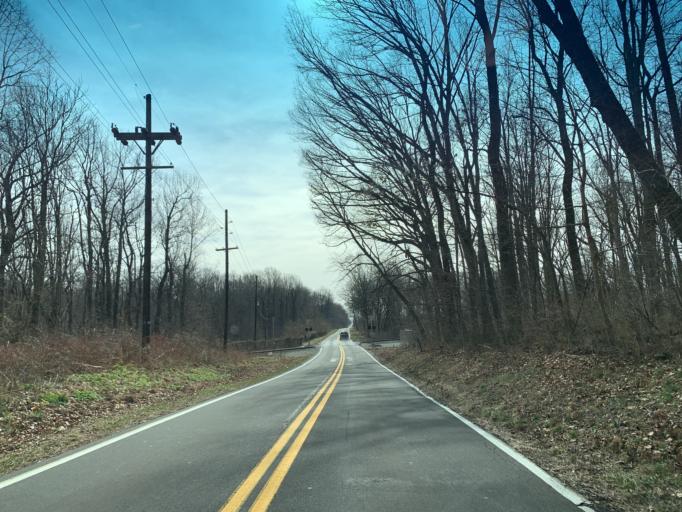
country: US
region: Maryland
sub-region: Frederick County
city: Adamstown
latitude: 39.3269
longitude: -77.4562
